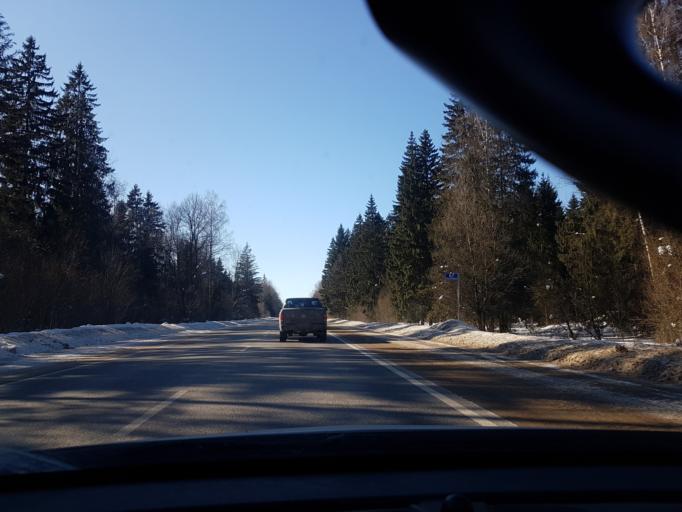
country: RU
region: Moskovskaya
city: Kostrovo
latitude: 55.9141
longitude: 36.7016
